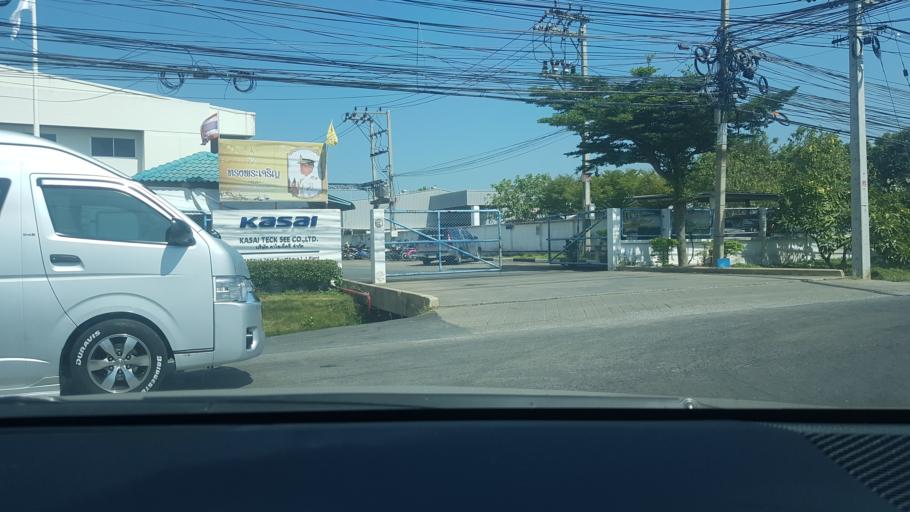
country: TH
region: Phra Nakhon Si Ayutthaya
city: Bang Pa-in
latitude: 14.2523
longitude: 100.6002
